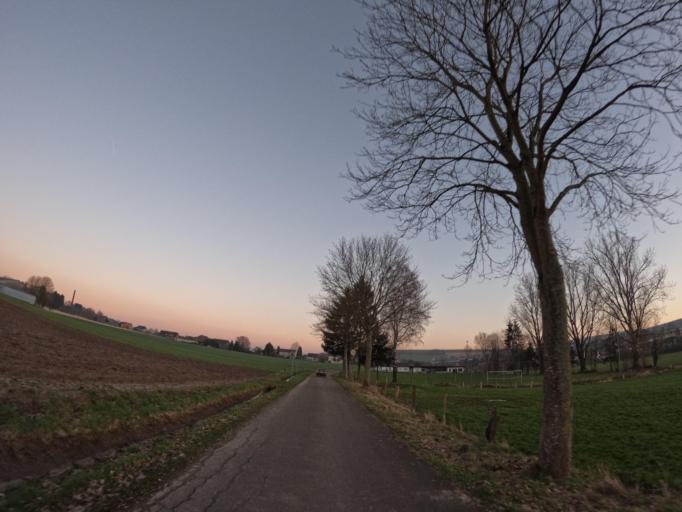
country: DE
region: Lower Saxony
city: Uslar
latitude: 51.6747
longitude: 9.5956
